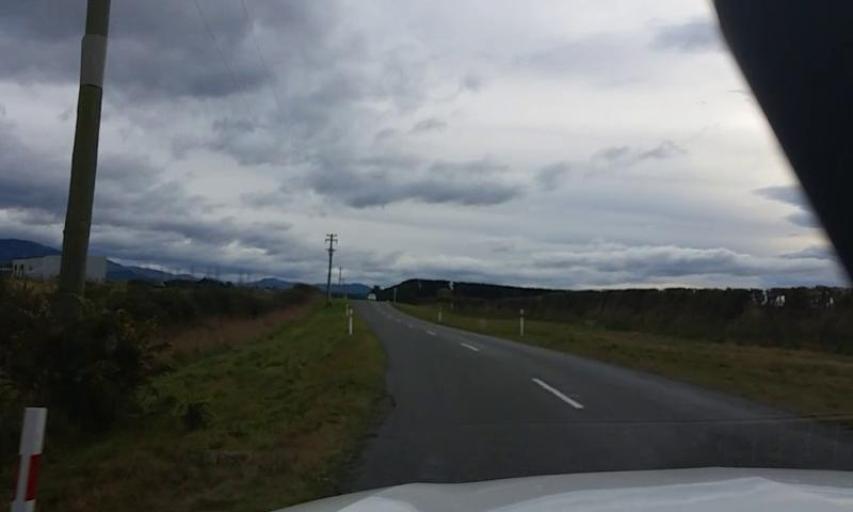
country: NZ
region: Canterbury
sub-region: Waimakariri District
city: Kaiapoi
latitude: -43.2959
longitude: 172.4376
